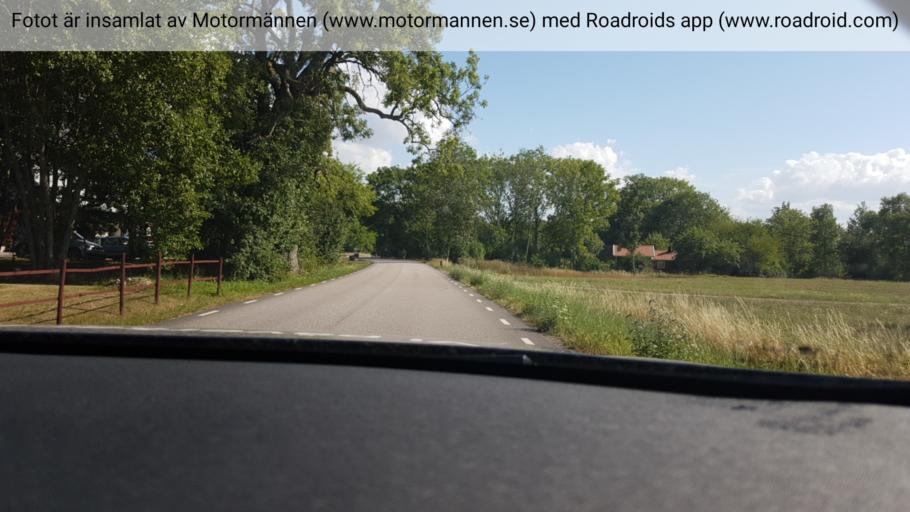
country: SE
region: Vaestra Goetaland
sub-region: Gotene Kommun
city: Kallby
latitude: 58.5340
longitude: 13.3220
